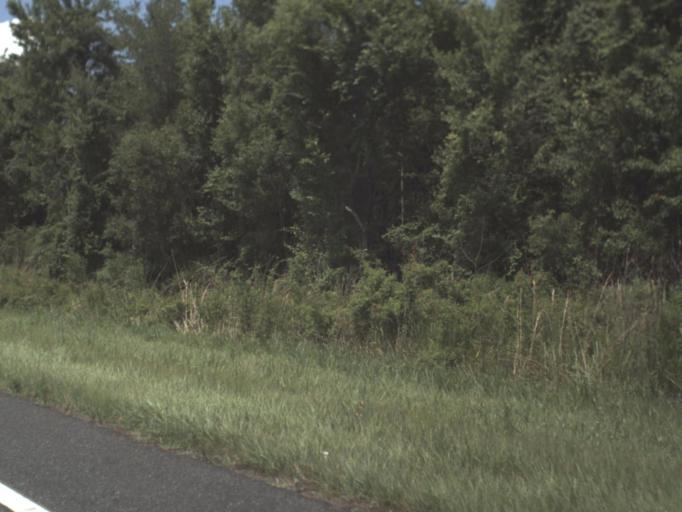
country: US
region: Florida
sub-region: Taylor County
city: Perry
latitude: 30.2632
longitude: -83.7117
